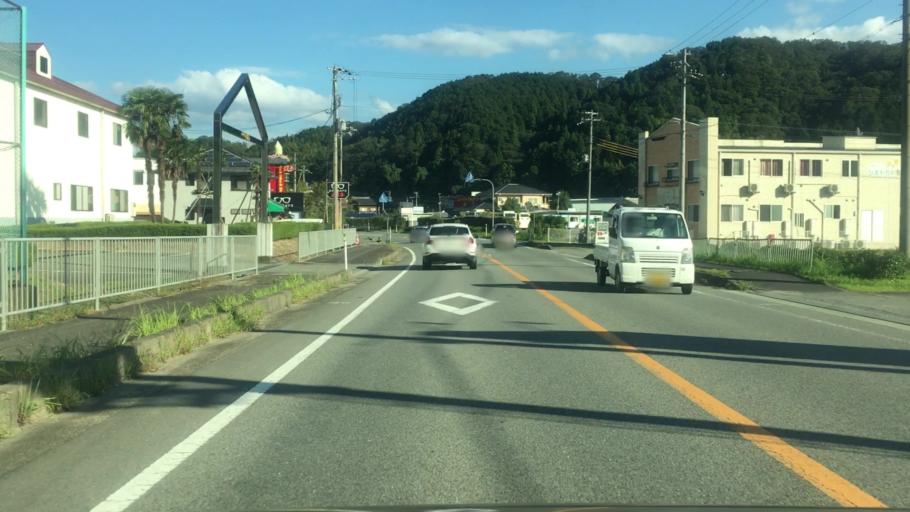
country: JP
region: Hyogo
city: Toyooka
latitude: 35.5555
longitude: 134.8334
